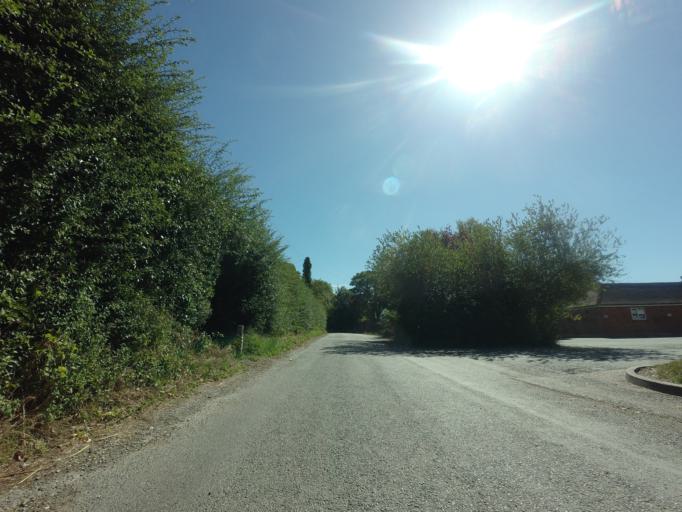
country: GB
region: England
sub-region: Kent
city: Ash
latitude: 51.3031
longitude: 1.2287
